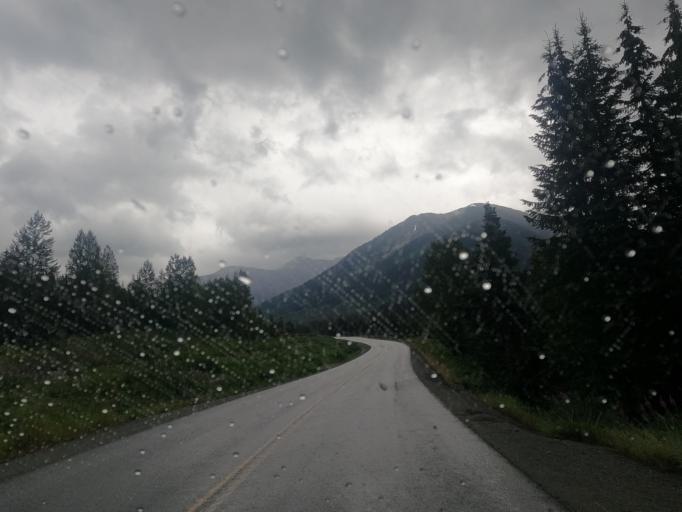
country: CA
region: British Columbia
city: Pemberton
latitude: 50.3836
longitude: -122.4254
